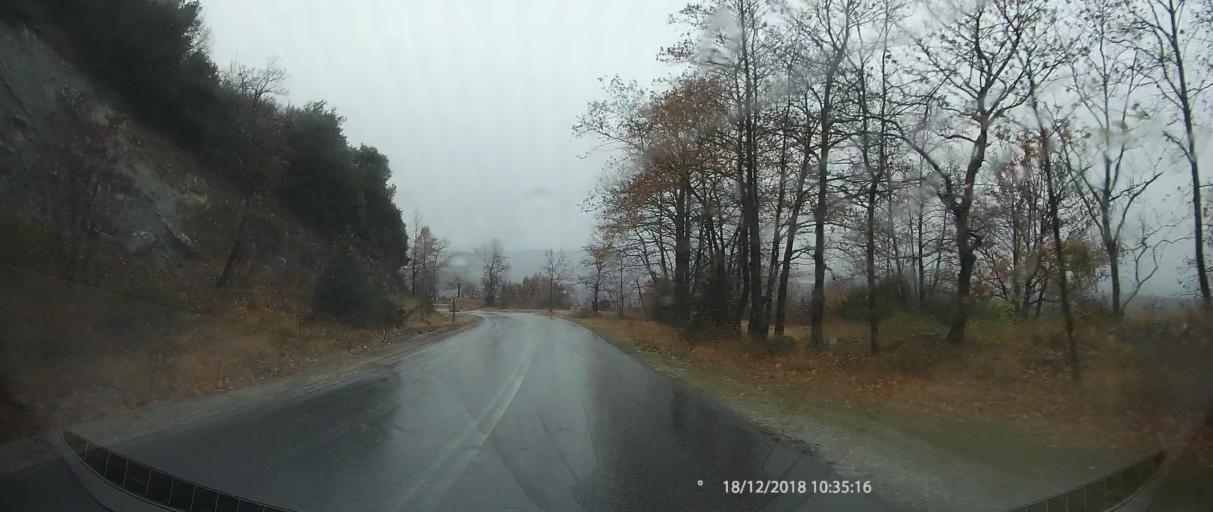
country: GR
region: Central Macedonia
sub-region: Nomos Pierias
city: Kato Milia
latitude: 40.2136
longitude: 22.3068
